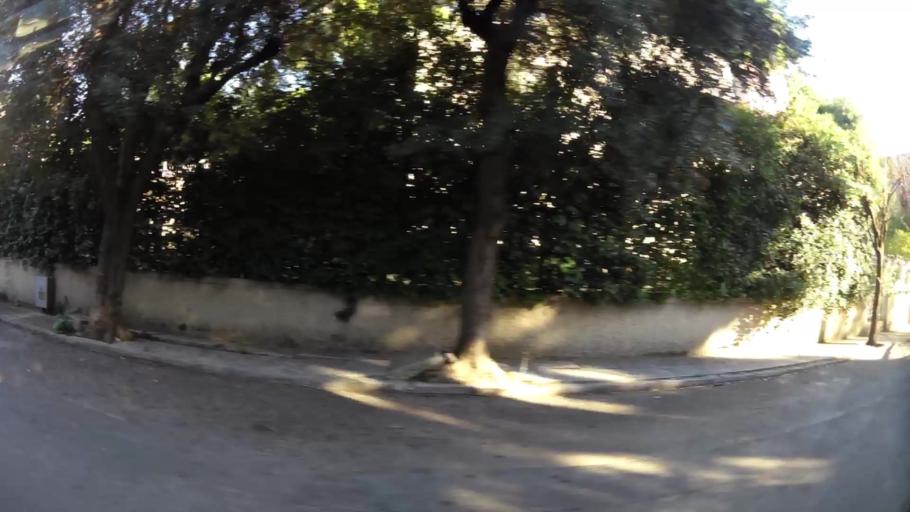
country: GR
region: Attica
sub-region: Nomarchia Athinas
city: Kifisia
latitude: 38.0817
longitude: 23.8054
